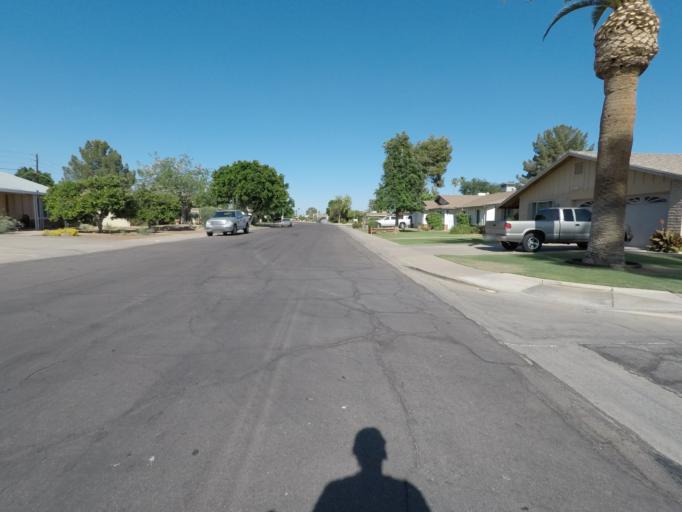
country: US
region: Arizona
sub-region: Maricopa County
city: Tempe
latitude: 33.3983
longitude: -111.9142
